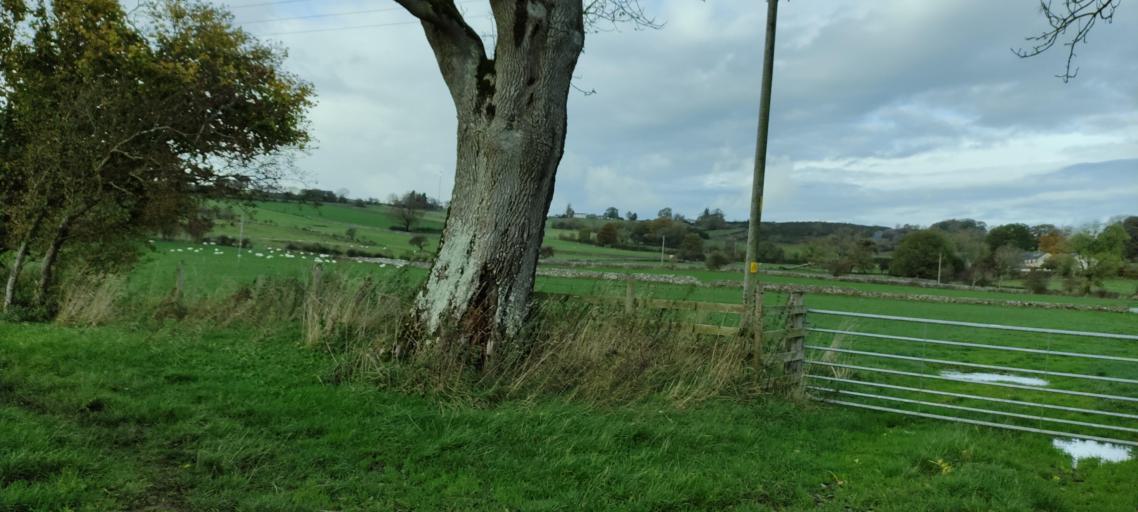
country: GB
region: England
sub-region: Cumbria
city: Wigton
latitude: 54.7503
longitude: -3.0598
